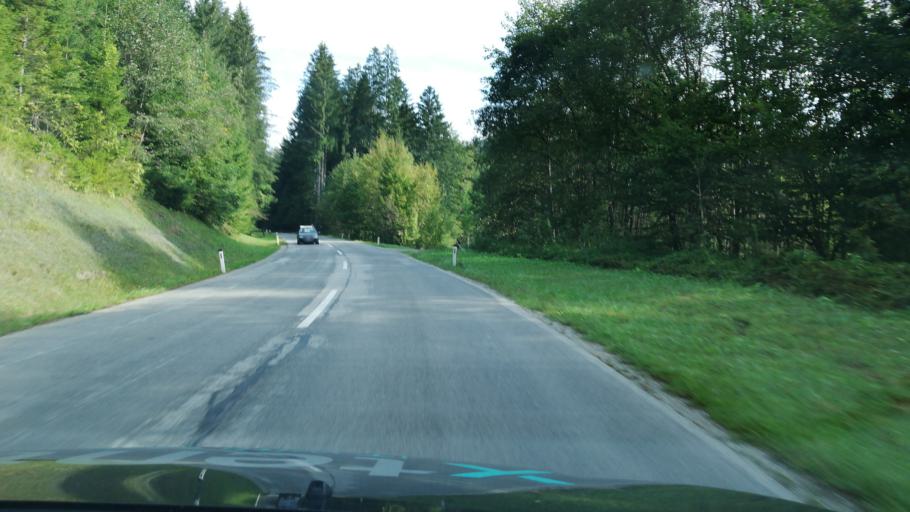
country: AT
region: Upper Austria
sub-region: Politischer Bezirk Steyr-Land
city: Maria Neustift
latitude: 47.9328
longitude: 14.6110
